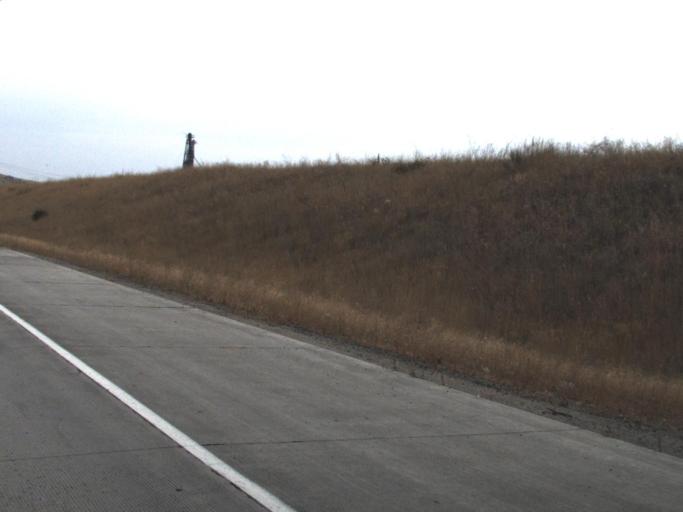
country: US
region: Washington
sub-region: Spokane County
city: Mead
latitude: 47.7599
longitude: -117.3658
